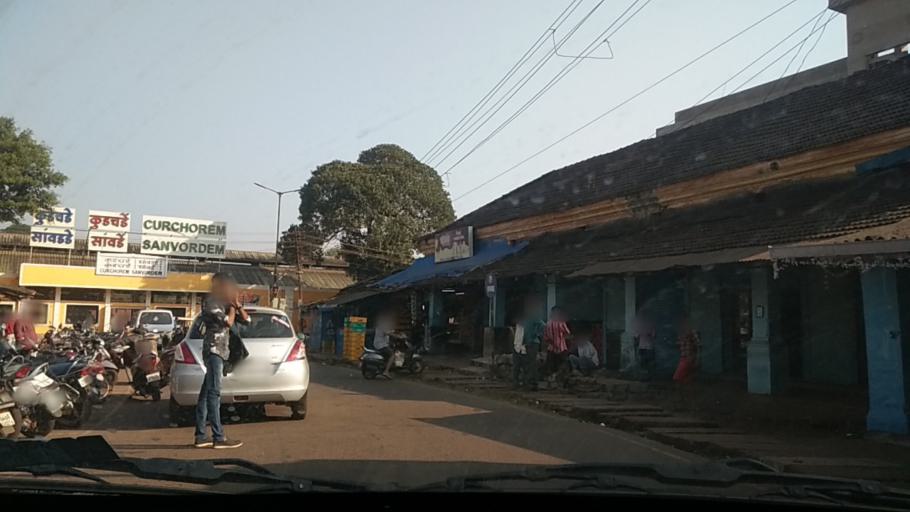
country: IN
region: Goa
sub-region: South Goa
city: Curchorem
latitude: 15.2636
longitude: 74.1086
